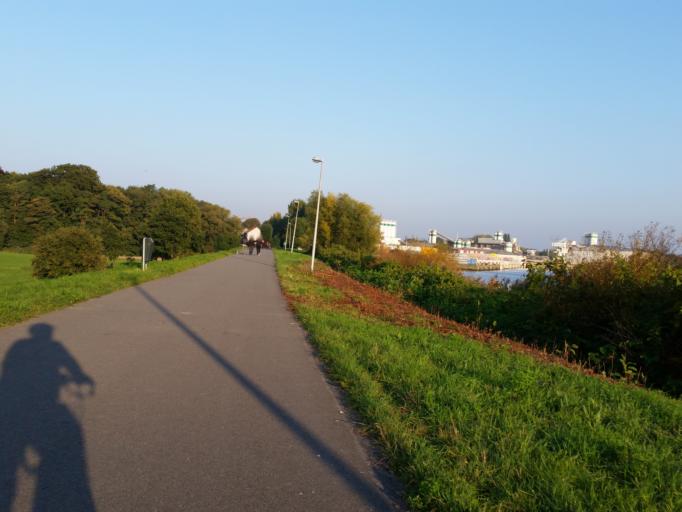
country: BE
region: Flanders
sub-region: Provincie Antwerpen
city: Niel
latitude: 51.1054
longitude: 4.3177
